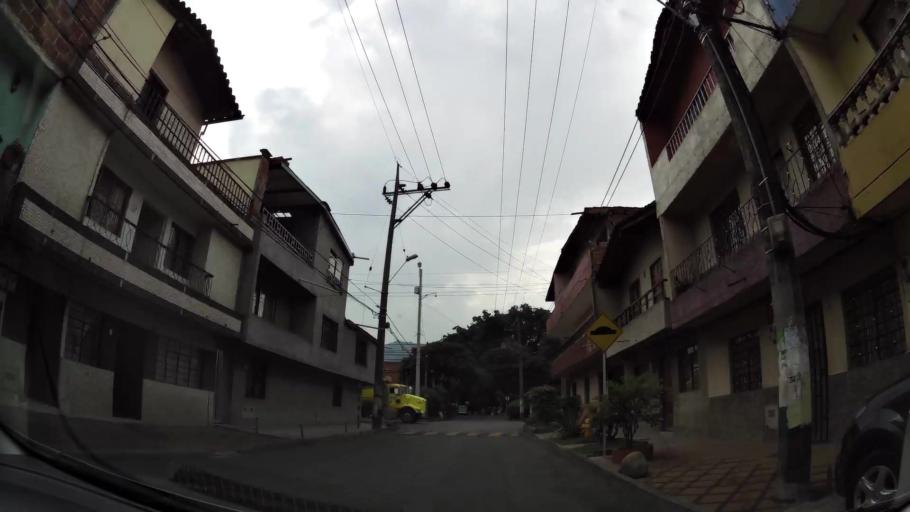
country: CO
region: Antioquia
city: Itagui
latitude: 6.1945
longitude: -75.5884
